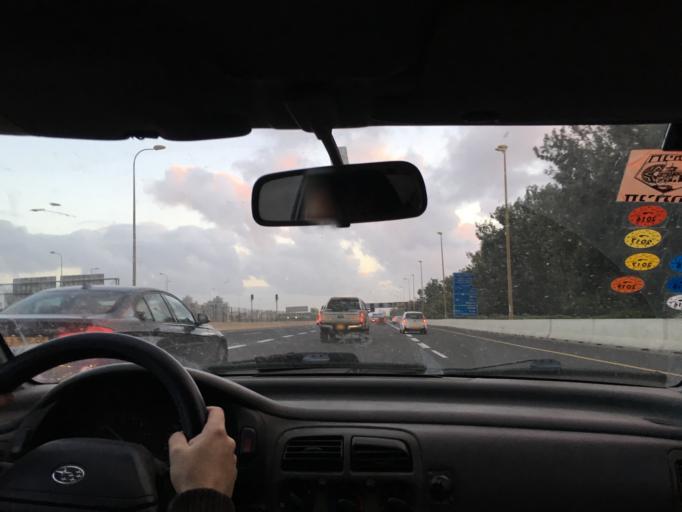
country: IL
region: Tel Aviv
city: Ramat HaSharon
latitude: 32.1335
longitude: 34.8097
